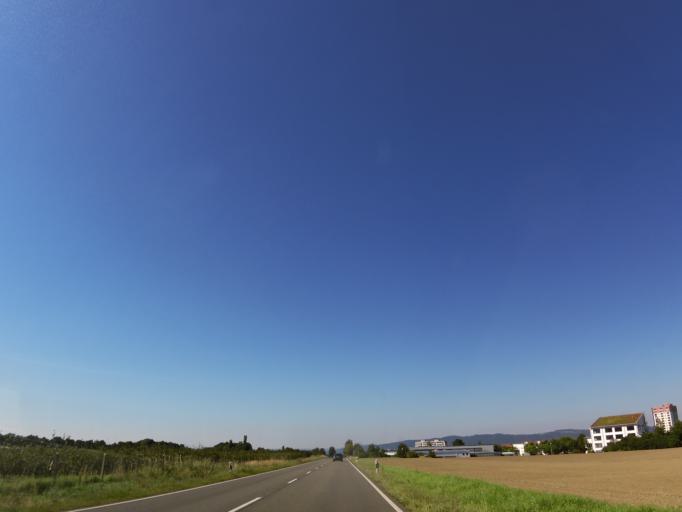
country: DE
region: Saxony
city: Pirna
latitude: 50.9449
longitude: 13.9579
